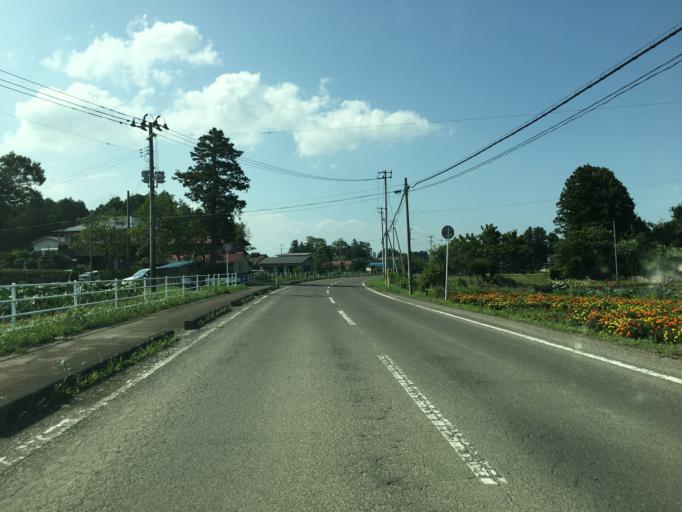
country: JP
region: Miyagi
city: Kakuda
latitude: 37.9477
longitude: 140.7976
